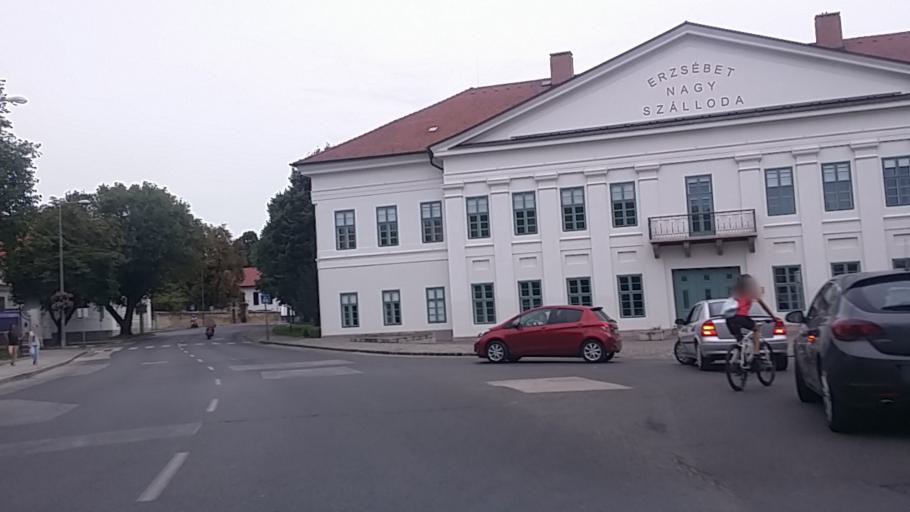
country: HU
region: Tolna
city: Paks
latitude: 46.6273
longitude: 18.8672
